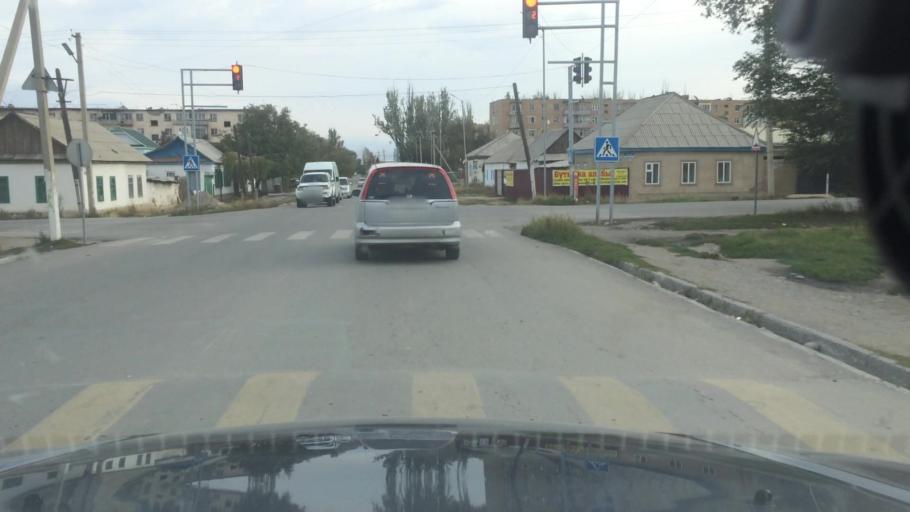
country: KG
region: Ysyk-Koel
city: Karakol
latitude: 42.4945
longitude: 78.3895
